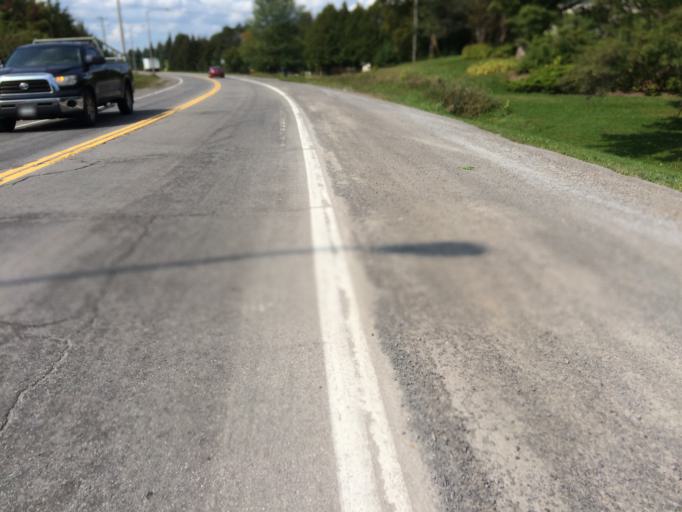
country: CA
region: Ontario
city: Bells Corners
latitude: 45.2146
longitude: -75.6657
